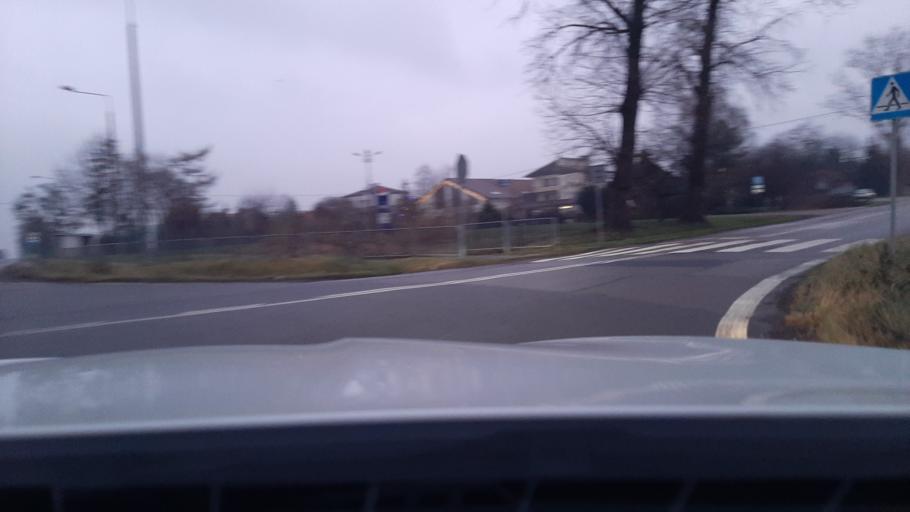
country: PL
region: Lublin Voivodeship
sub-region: Powiat lubelski
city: Garbow
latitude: 51.3440
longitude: 22.3633
